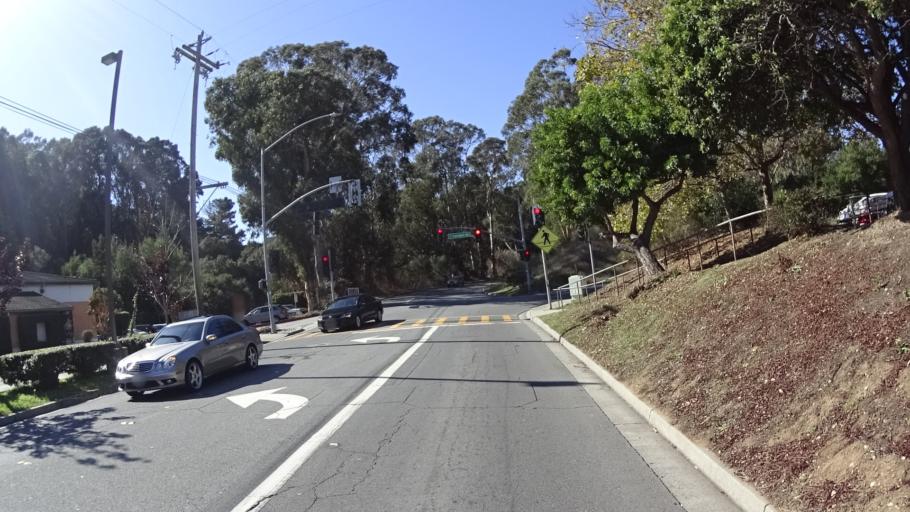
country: US
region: California
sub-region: San Mateo County
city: San Bruno
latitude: 37.6140
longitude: -122.4198
